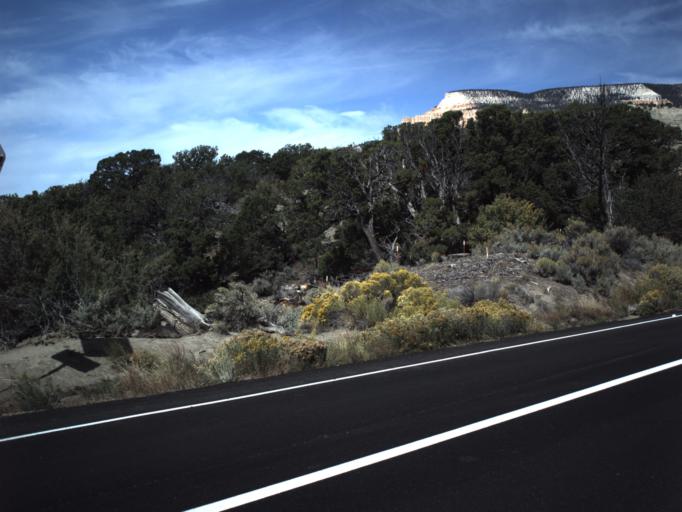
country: US
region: Utah
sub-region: Garfield County
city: Panguitch
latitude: 37.6403
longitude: -111.8443
